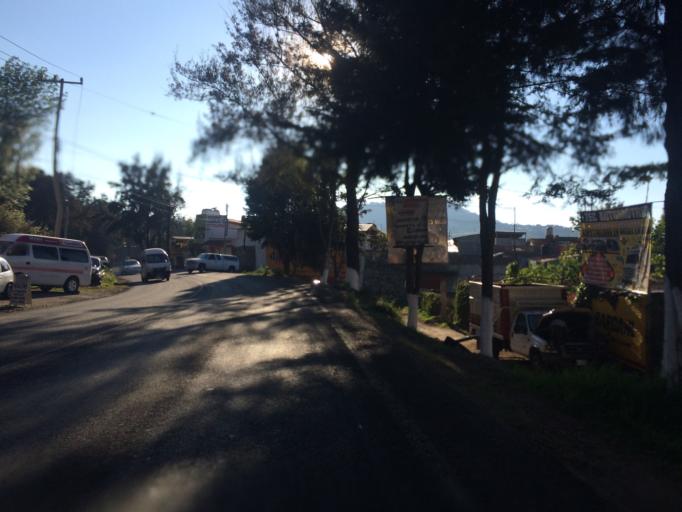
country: MX
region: Michoacan
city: Patzcuaro
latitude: 19.5063
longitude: -101.6107
